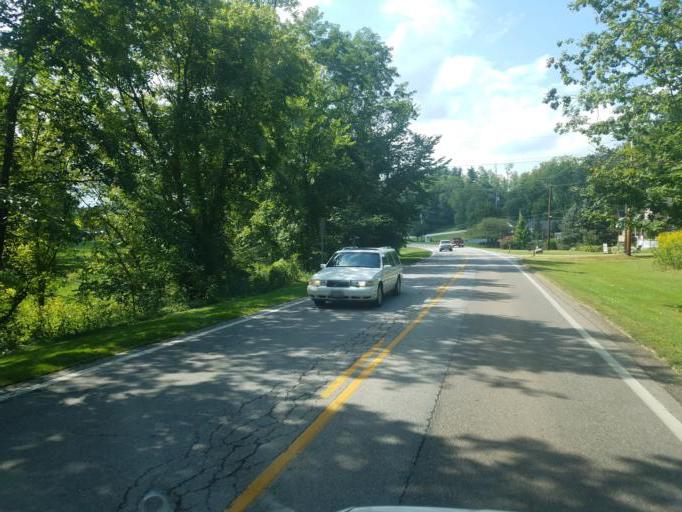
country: US
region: Ohio
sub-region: Sandusky County
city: Bellville
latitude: 40.6236
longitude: -82.5072
